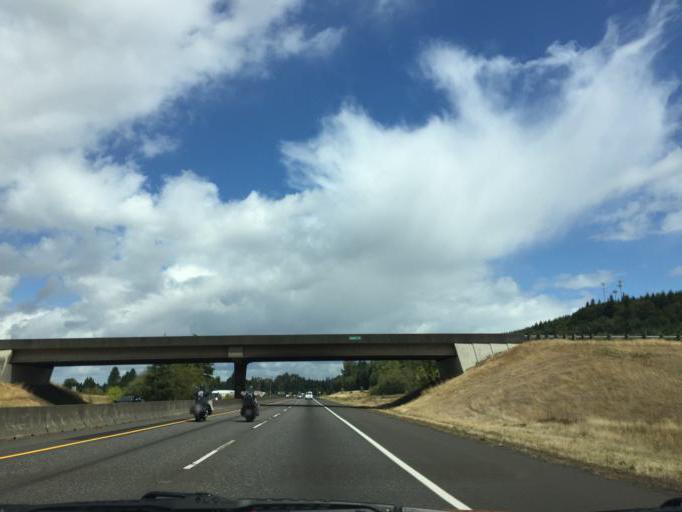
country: US
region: Washington
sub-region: Lewis County
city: Winlock
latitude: 46.3896
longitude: -122.9022
